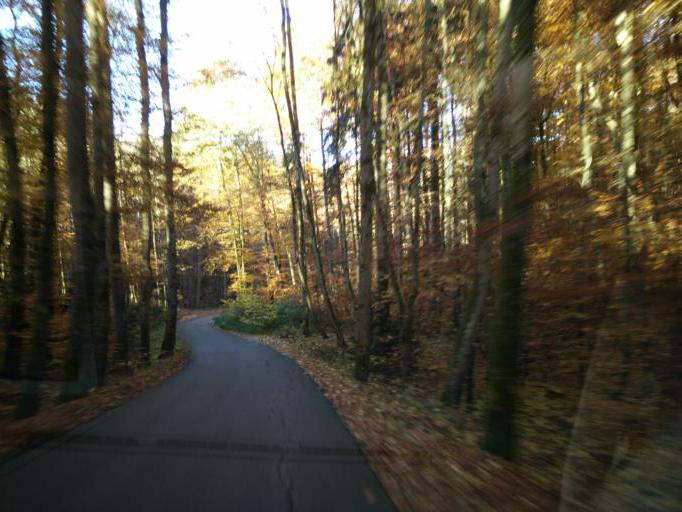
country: DE
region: Baden-Wuerttemberg
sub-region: Tuebingen Region
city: Gomaringen
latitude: 48.4269
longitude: 9.1078
